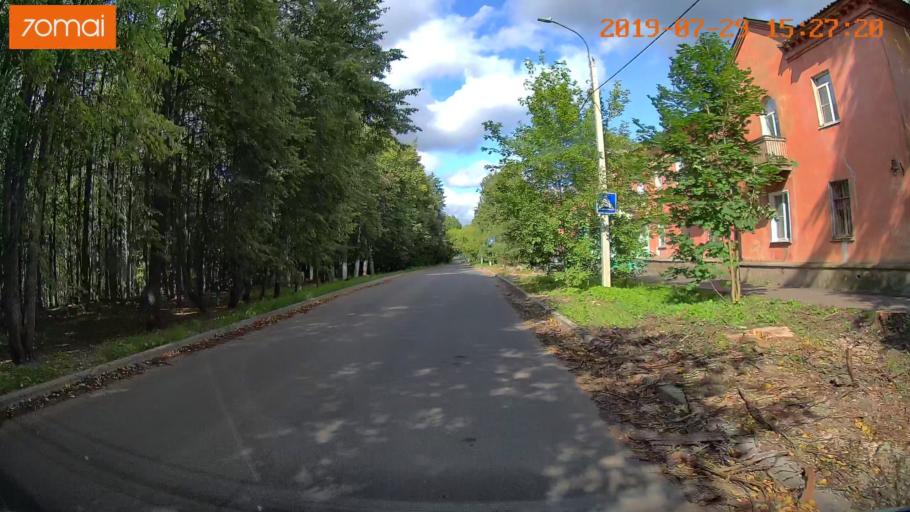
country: RU
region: Ivanovo
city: Bogorodskoye
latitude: 57.0218
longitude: 41.0072
